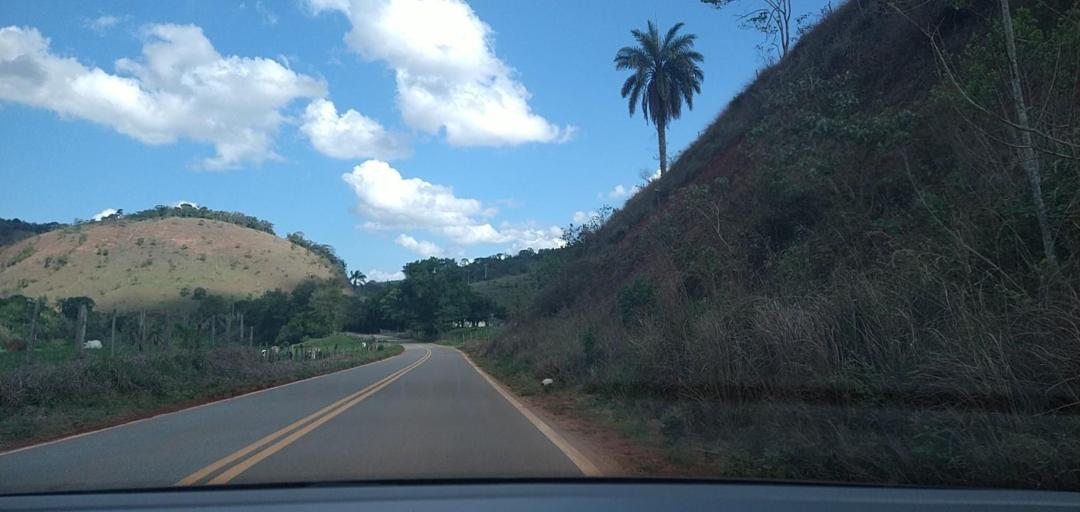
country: BR
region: Minas Gerais
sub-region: Rio Piracicaba
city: Rio Piracicaba
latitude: -19.9922
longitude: -43.1176
